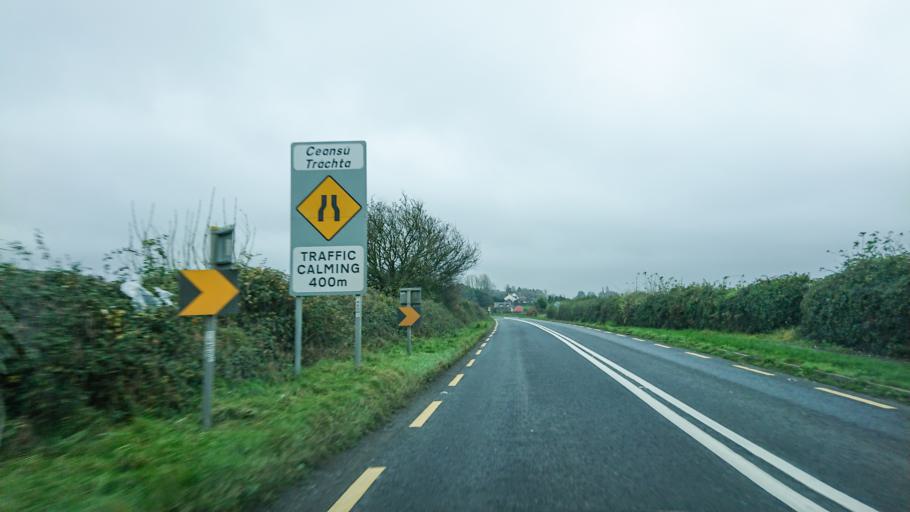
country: IE
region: Leinster
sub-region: Kilkenny
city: Mooncoin
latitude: 52.3006
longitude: -7.2695
